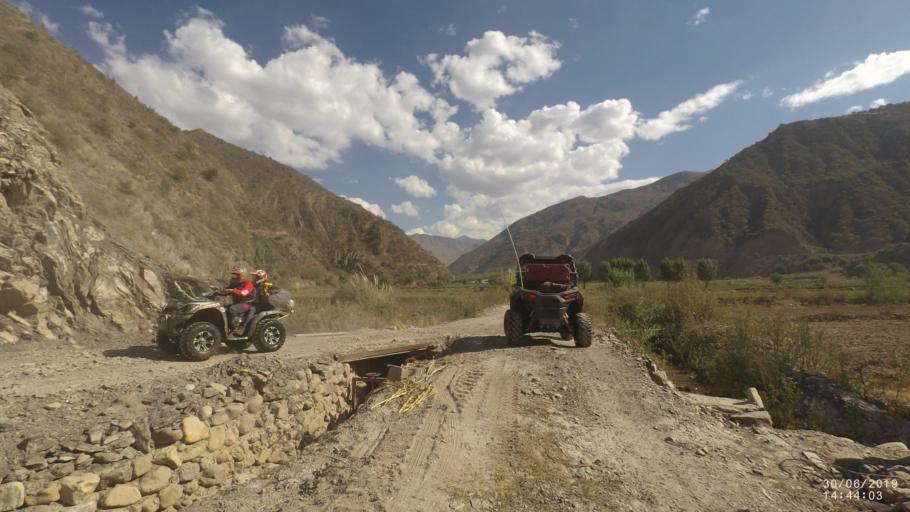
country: BO
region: Cochabamba
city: Irpa Irpa
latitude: -17.8010
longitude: -66.3505
